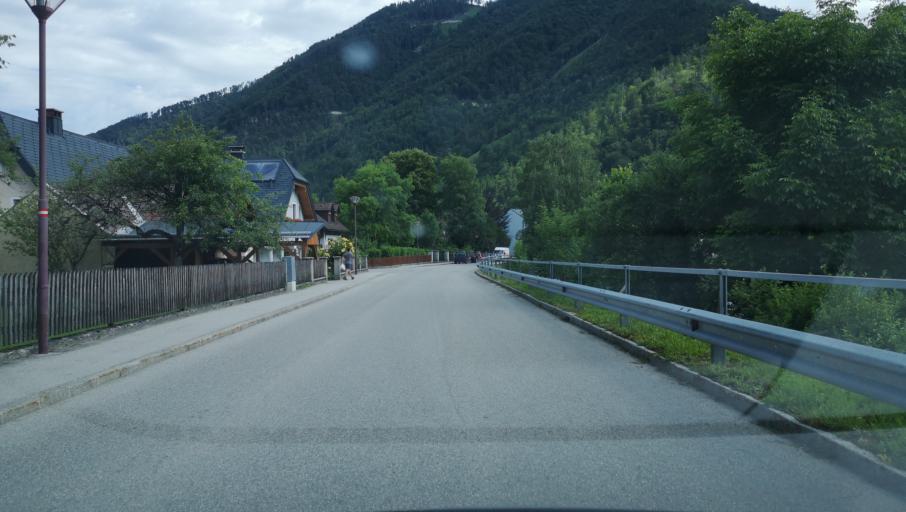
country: AT
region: Lower Austria
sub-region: Politischer Bezirk Amstetten
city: Hollenstein an der Ybbs
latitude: 47.8015
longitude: 14.7710
